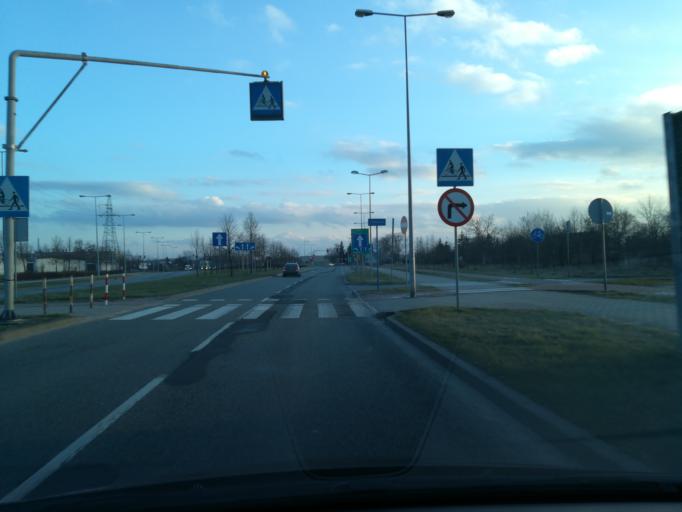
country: PL
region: Lodz Voivodeship
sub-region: Piotrkow Trybunalski
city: Piotrkow Trybunalski
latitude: 51.4085
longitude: 19.6561
